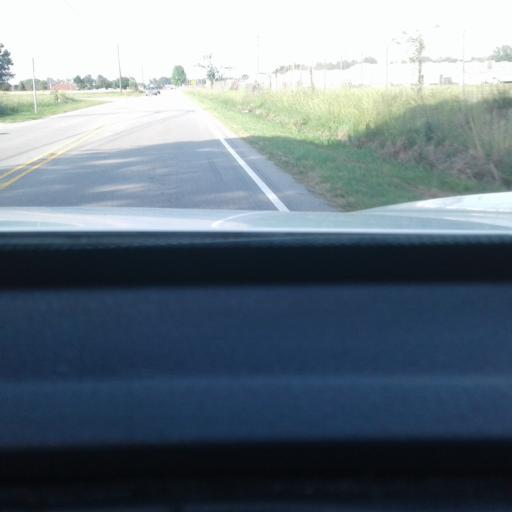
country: US
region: North Carolina
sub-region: Harnett County
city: Dunn
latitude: 35.3281
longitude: -78.5974
